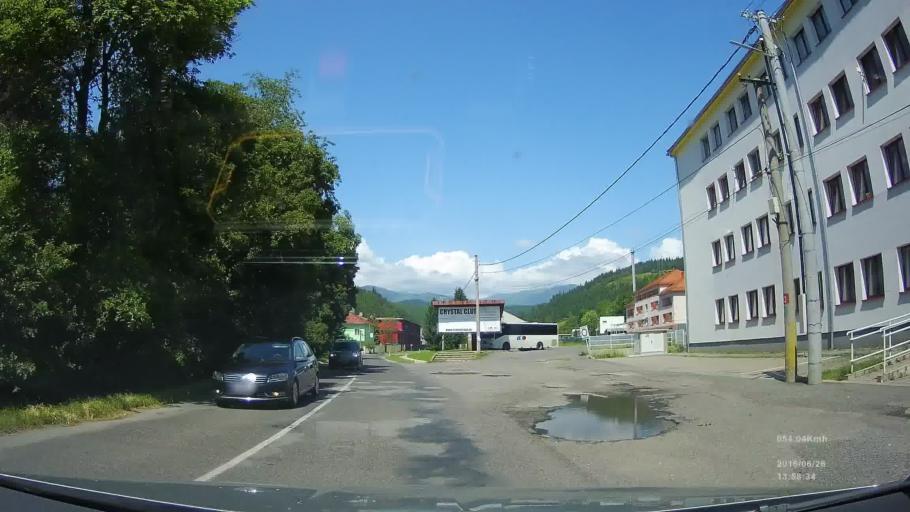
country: SK
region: Banskobystricky
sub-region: Okres Banska Bystrica
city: Brezno
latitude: 48.8113
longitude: 19.5573
